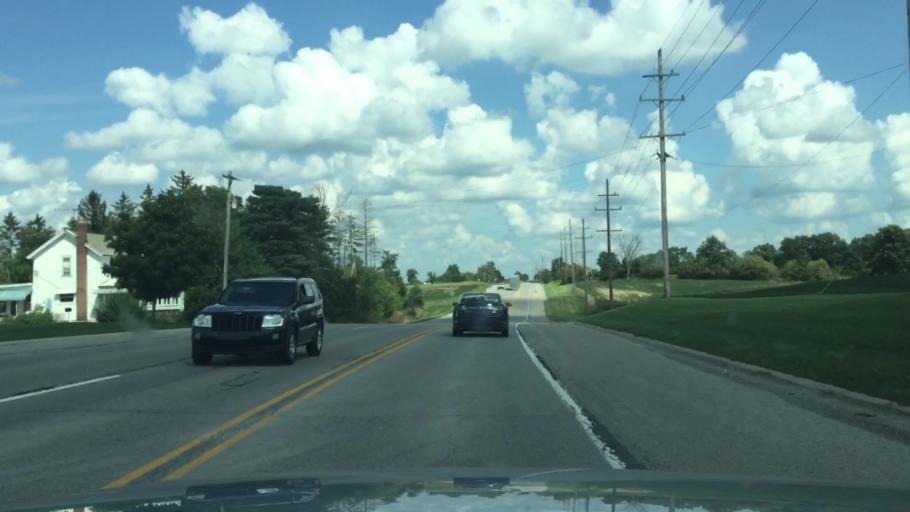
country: US
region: Michigan
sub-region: Washtenaw County
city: Saline
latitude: 42.1386
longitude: -83.8483
